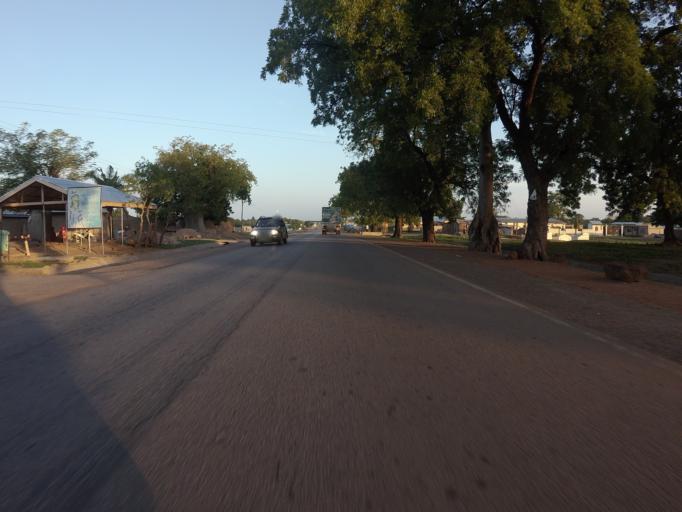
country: GH
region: Upper East
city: Navrongo
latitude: 10.9670
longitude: -1.1014
